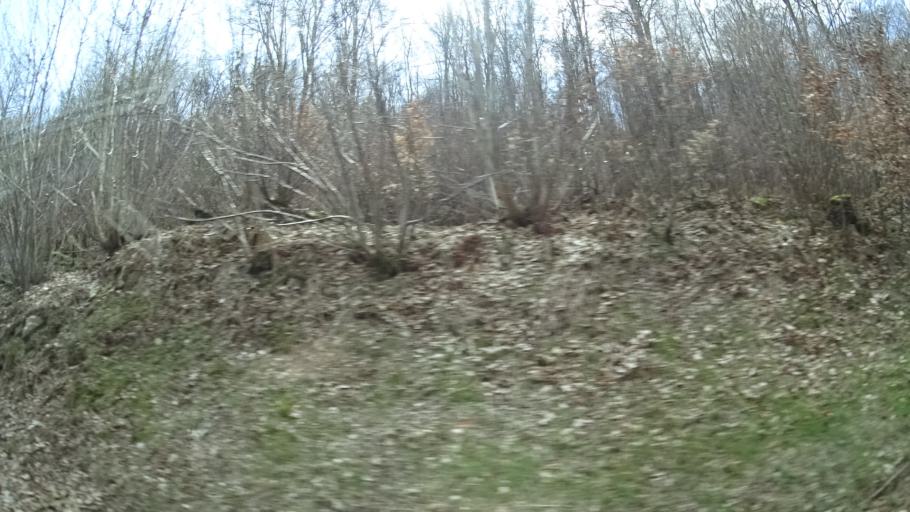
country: DE
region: Rheinland-Pfalz
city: Kirschweiler
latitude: 49.7647
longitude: 7.2302
